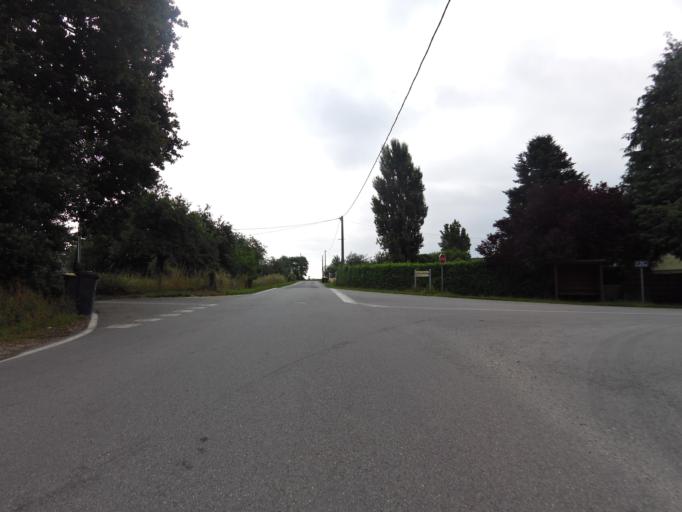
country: FR
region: Brittany
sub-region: Departement du Morbihan
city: Baden
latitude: 47.6150
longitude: -2.8955
